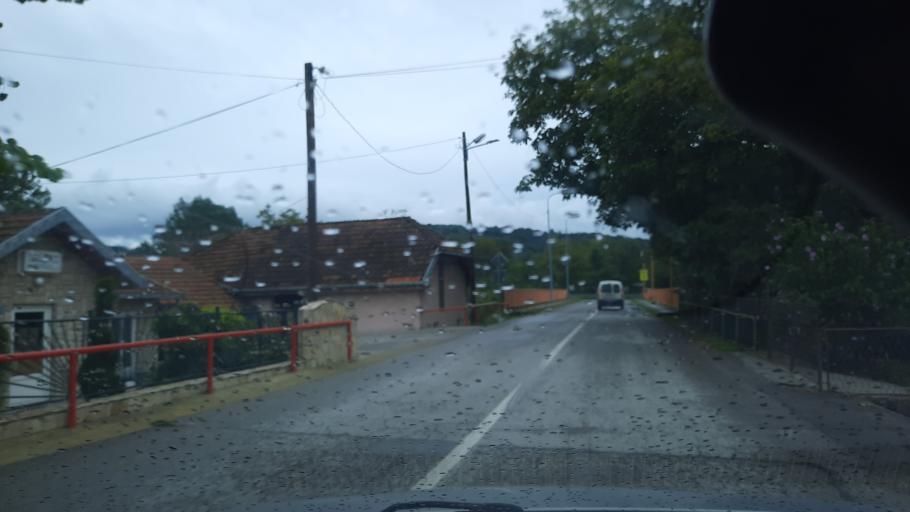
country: RS
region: Central Serbia
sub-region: Raski Okrug
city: Vrnjacka Banja
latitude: 43.7150
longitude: 20.8284
